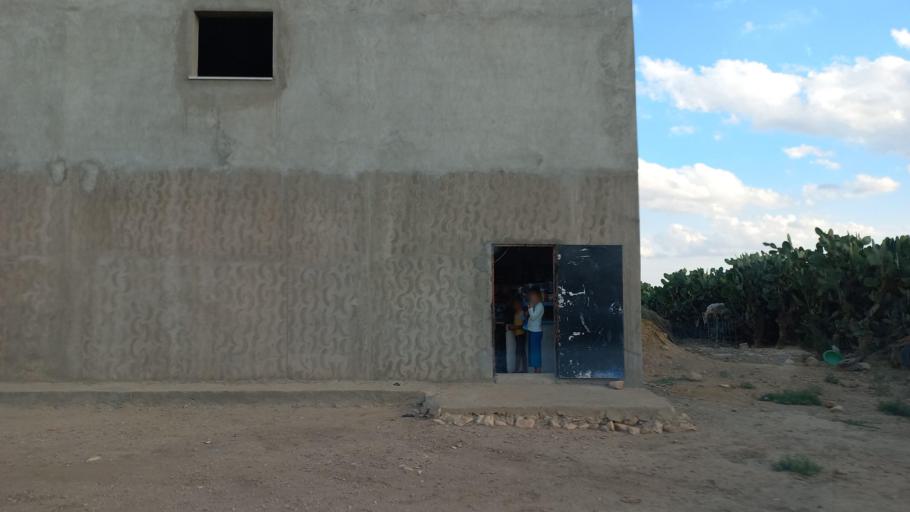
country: TN
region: Al Qasrayn
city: Sbiba
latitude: 35.3858
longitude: 9.0479
